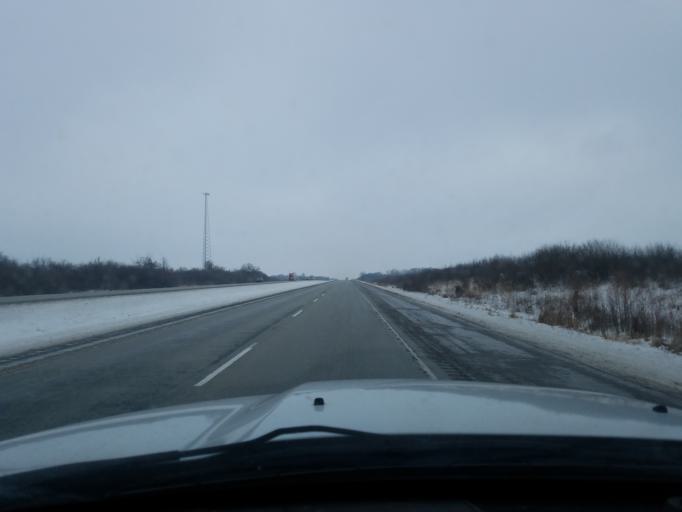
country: US
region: Indiana
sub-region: Fulton County
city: Rochester
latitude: 41.1378
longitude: -86.2397
